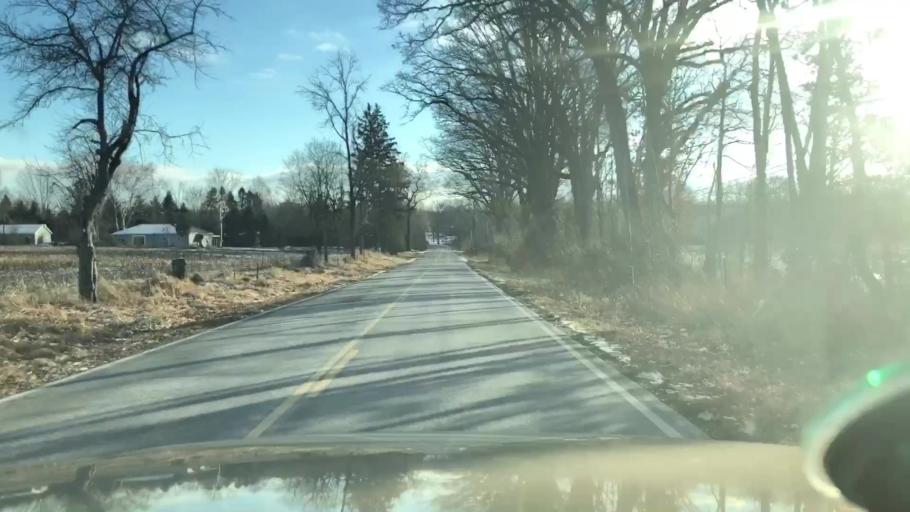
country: US
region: Michigan
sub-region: Jackson County
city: Vandercook Lake
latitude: 42.1649
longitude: -84.4523
